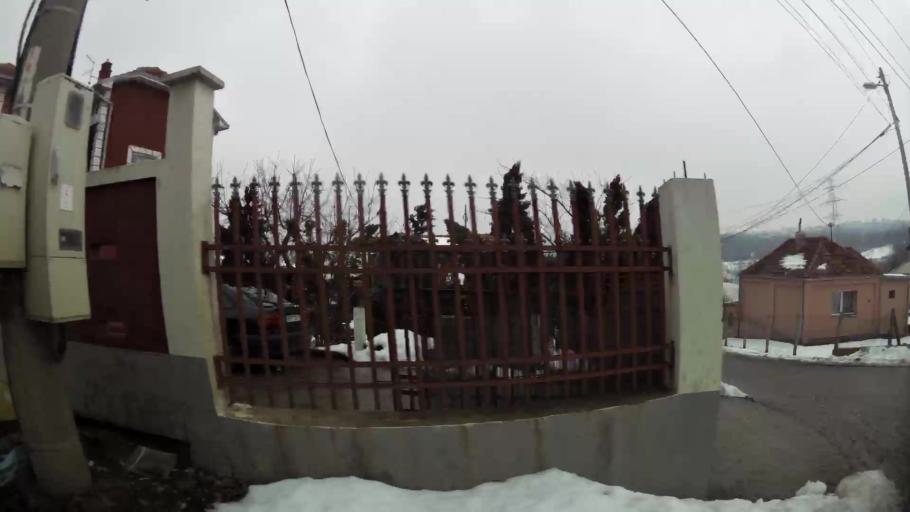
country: RS
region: Central Serbia
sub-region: Belgrade
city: Zvezdara
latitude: 44.7659
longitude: 20.5200
